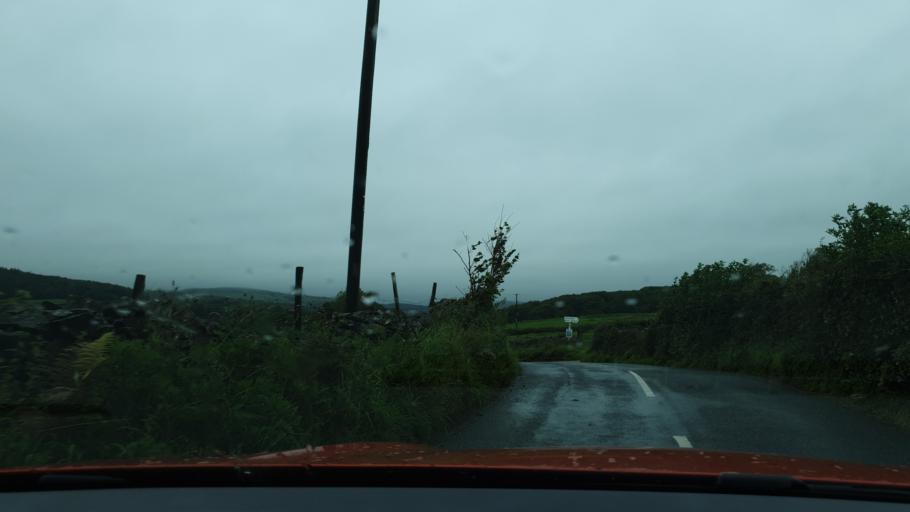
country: GB
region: England
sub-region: Cumbria
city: Ulverston
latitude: 54.2502
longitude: -3.0546
